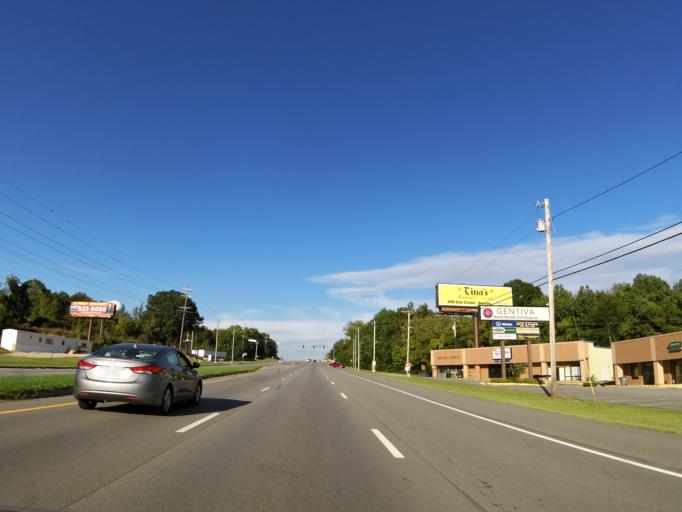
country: US
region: Alabama
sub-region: Lauderdale County
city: East Florence
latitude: 34.8346
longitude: -87.6110
